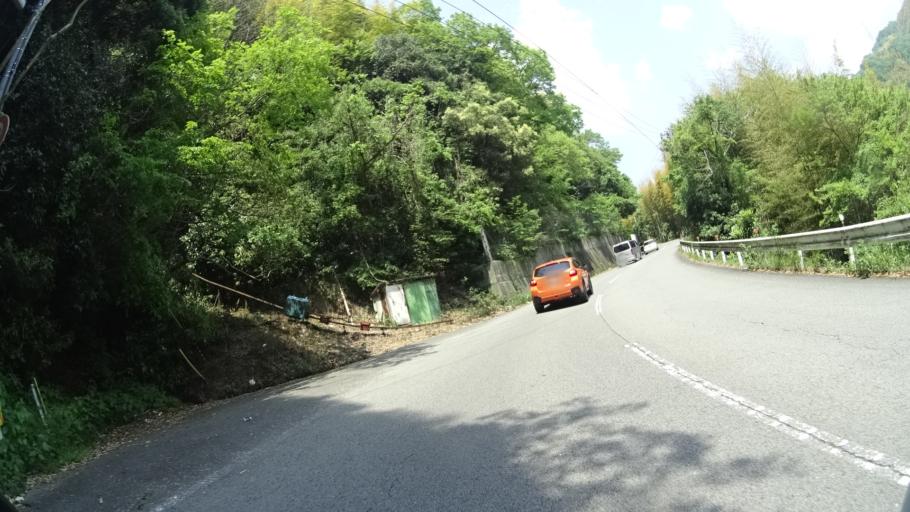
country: JP
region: Ehime
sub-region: Shikoku-chuo Shi
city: Matsuyama
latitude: 33.8763
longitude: 132.8355
